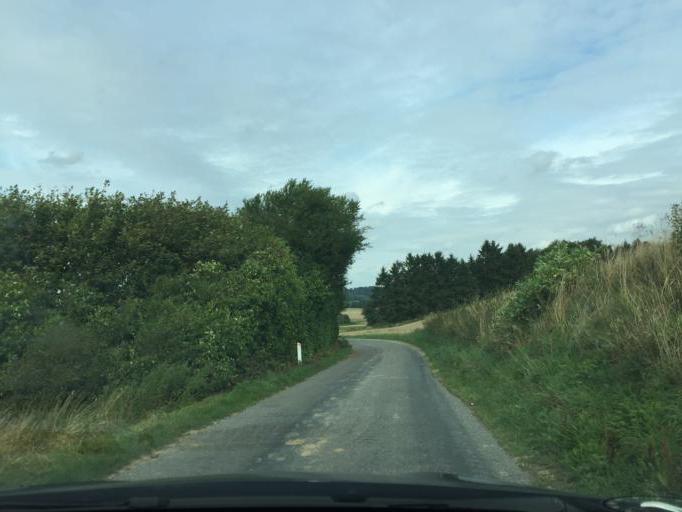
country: DK
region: South Denmark
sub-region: Assens Kommune
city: Vissenbjerg
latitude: 55.3542
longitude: 10.1182
